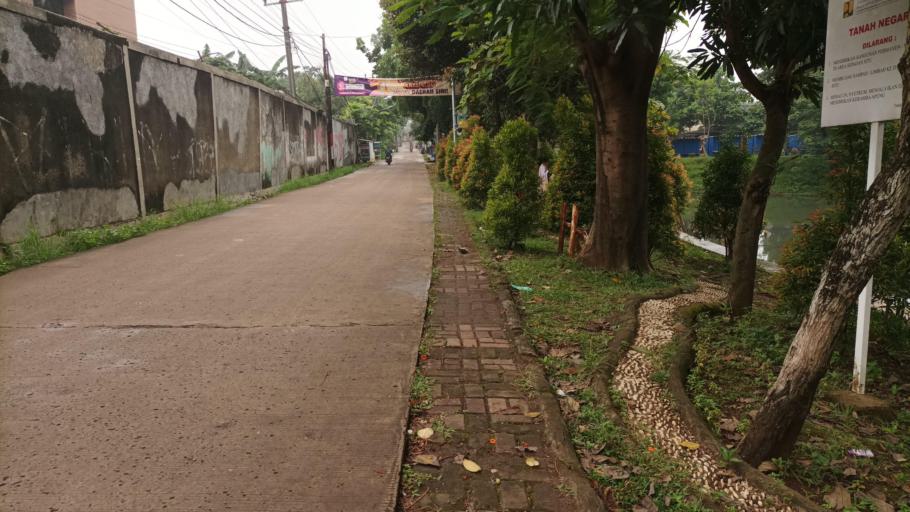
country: ID
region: West Java
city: Cileungsir
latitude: -6.3895
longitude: 106.9157
